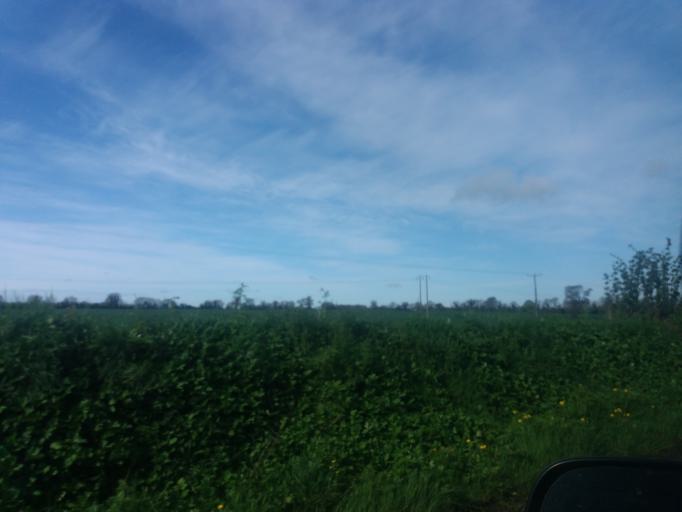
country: IE
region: Leinster
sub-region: An Mhi
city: Kells
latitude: 53.7227
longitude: -6.8563
